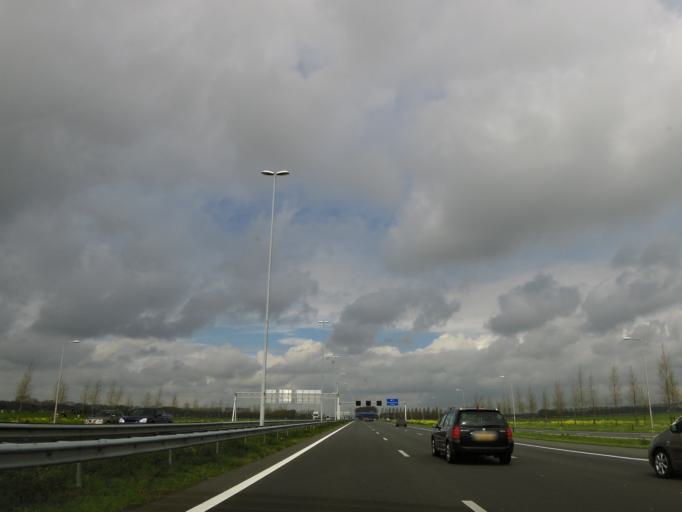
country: NL
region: Gelderland
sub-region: Gemeente Zaltbommel
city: Zaltbommel
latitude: 51.8639
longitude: 5.2226
